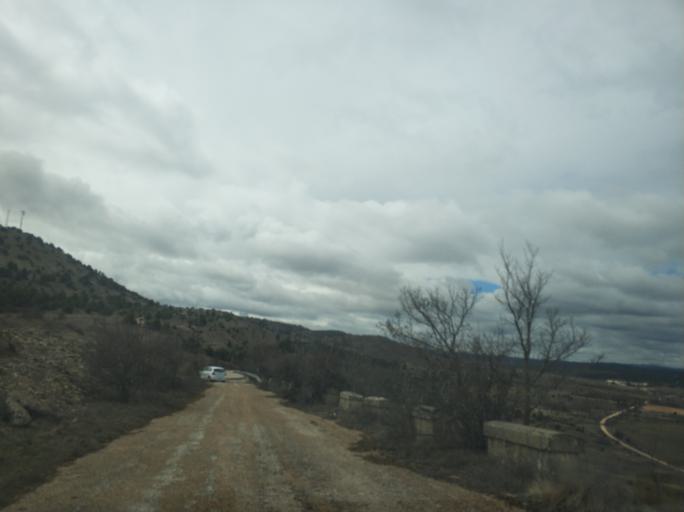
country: ES
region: Castille and Leon
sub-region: Provincia de Soria
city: Abejar
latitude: 41.7979
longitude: -2.7687
